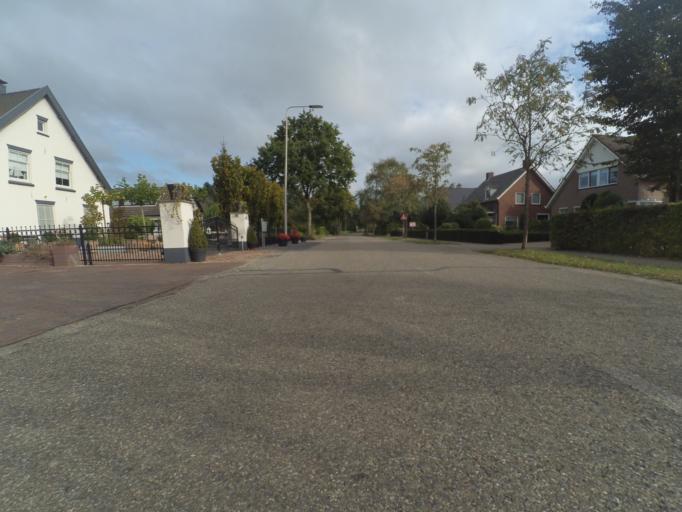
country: NL
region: Utrecht
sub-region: Gemeente Utrechtse Heuvelrug
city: Amerongen
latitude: 51.9664
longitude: 5.4537
